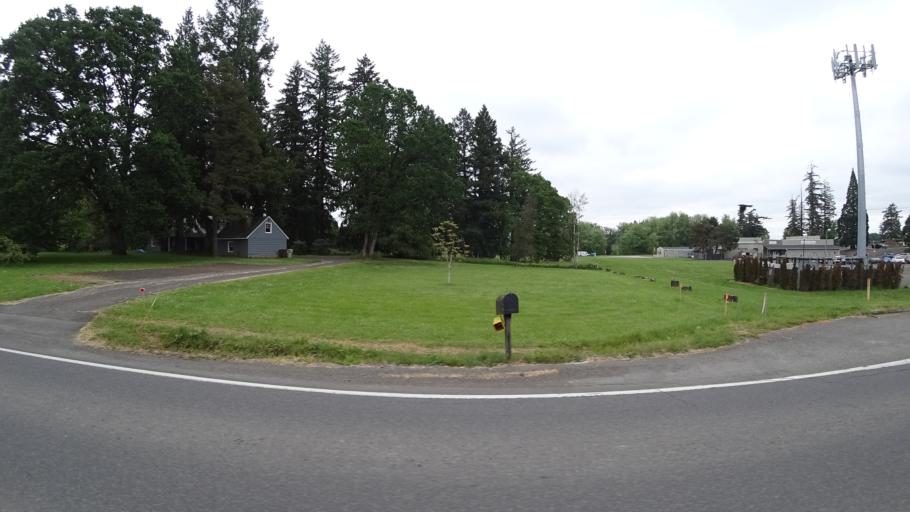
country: US
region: Oregon
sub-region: Washington County
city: Rockcreek
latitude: 45.5683
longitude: -122.8956
